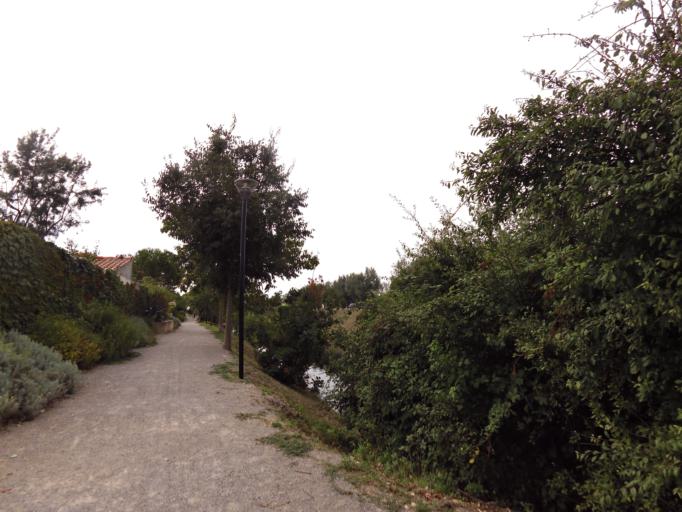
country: FR
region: Languedoc-Roussillon
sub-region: Departement de l'Herault
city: Lunel
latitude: 43.6662
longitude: 4.1284
